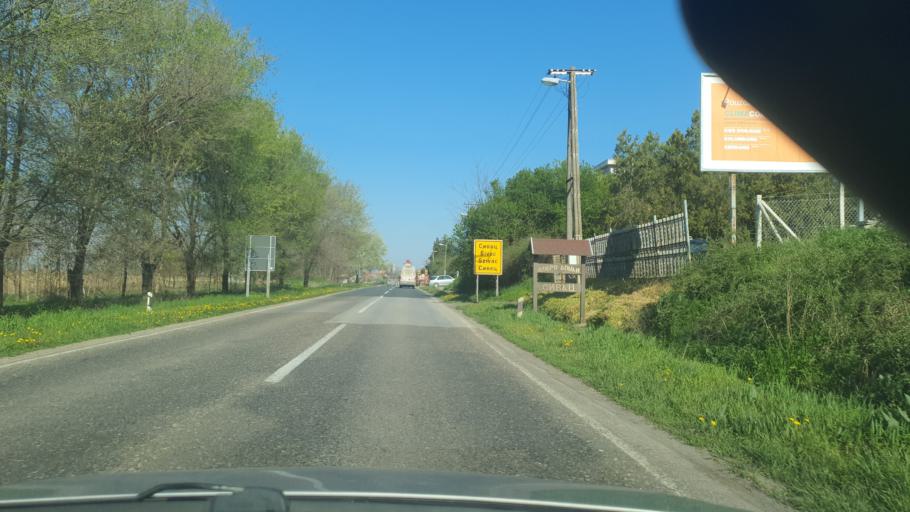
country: RS
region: Autonomna Pokrajina Vojvodina
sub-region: Zapadnobacki Okrug
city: Kula
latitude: 45.6855
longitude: 19.3954
